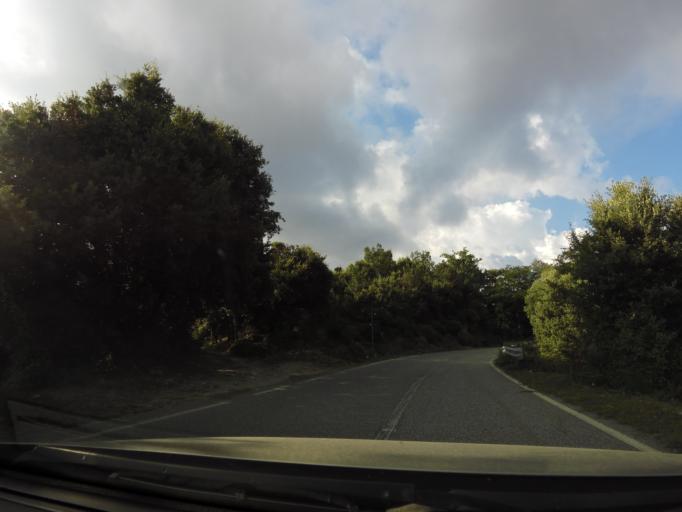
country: IT
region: Calabria
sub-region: Provincia di Vibo-Valentia
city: Nardodipace
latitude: 38.4795
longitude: 16.3822
